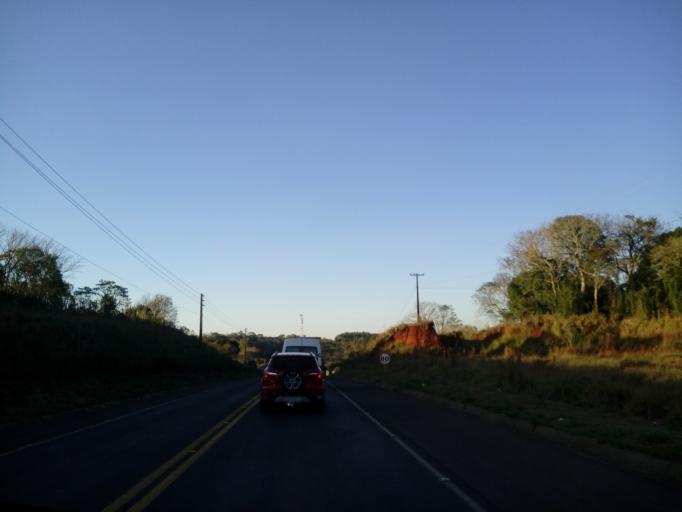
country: BR
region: Santa Catarina
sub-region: Chapeco
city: Chapeco
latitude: -27.2087
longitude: -52.6597
